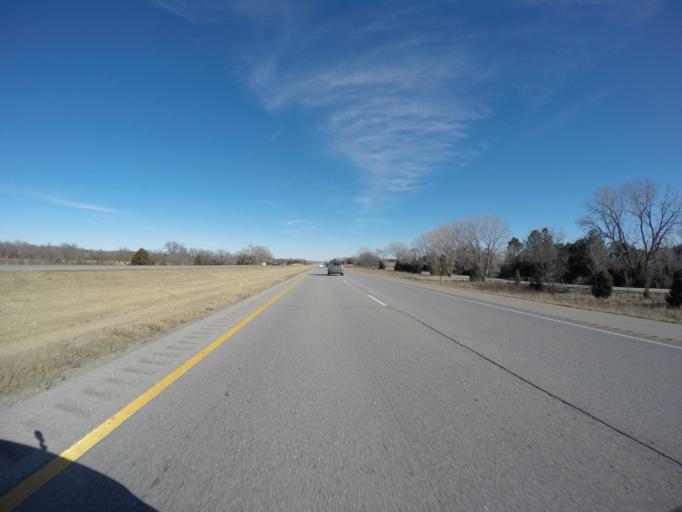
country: US
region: Nebraska
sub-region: Seward County
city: Milford
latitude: 40.8204
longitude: -96.9037
